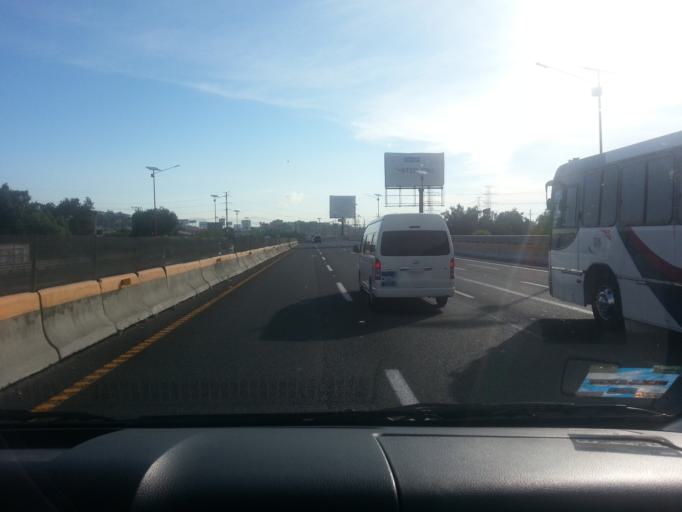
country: MX
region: Mexico
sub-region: Tlalnepantla de Baz
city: Puerto Escondido (Tepeolulco Puerto Escondido)
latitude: 19.5533
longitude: -99.0632
